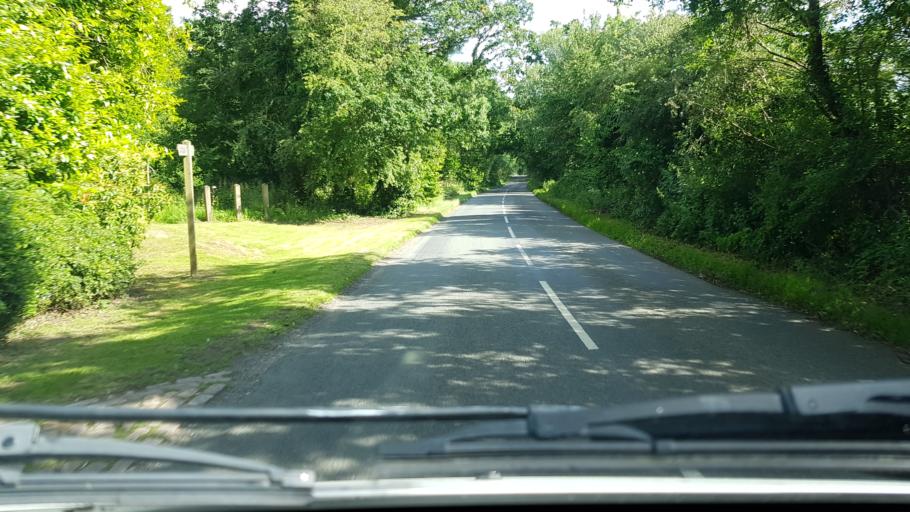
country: GB
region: England
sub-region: Worcestershire
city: Bewdley
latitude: 52.4028
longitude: -2.3058
